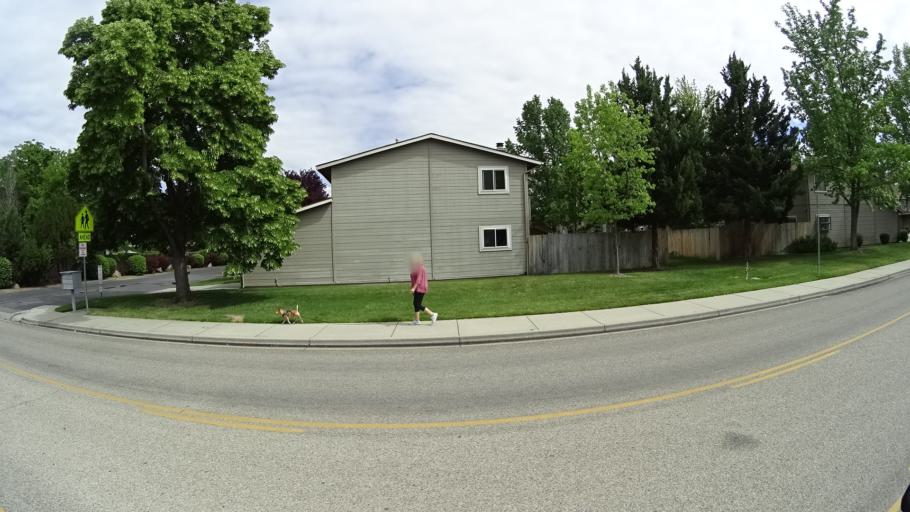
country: US
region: Idaho
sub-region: Ada County
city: Boise
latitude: 43.5788
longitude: -116.1823
